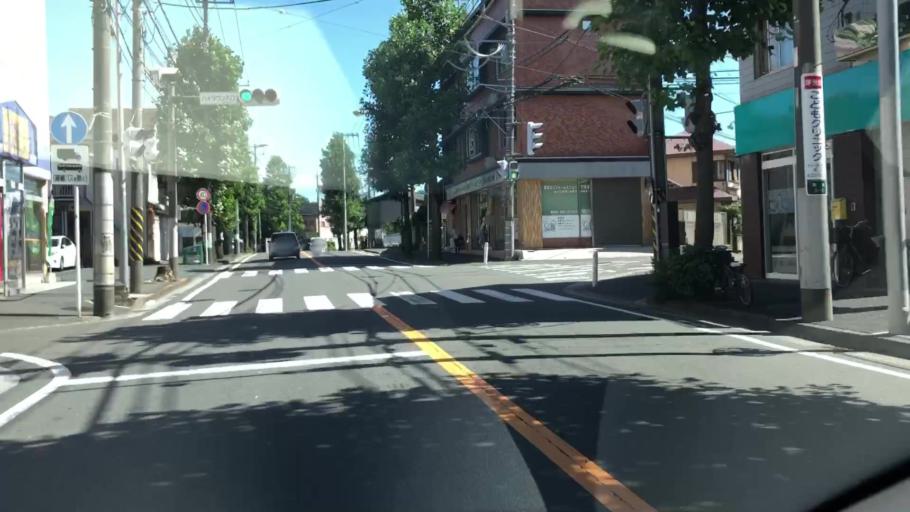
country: JP
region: Kanagawa
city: Yokohama
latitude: 35.3812
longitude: 139.6065
